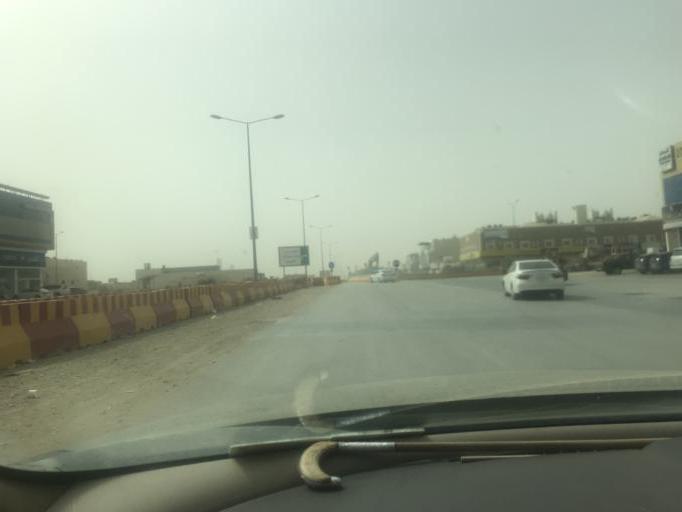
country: SA
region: Ar Riyad
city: Riyadh
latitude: 24.8125
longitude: 46.5995
